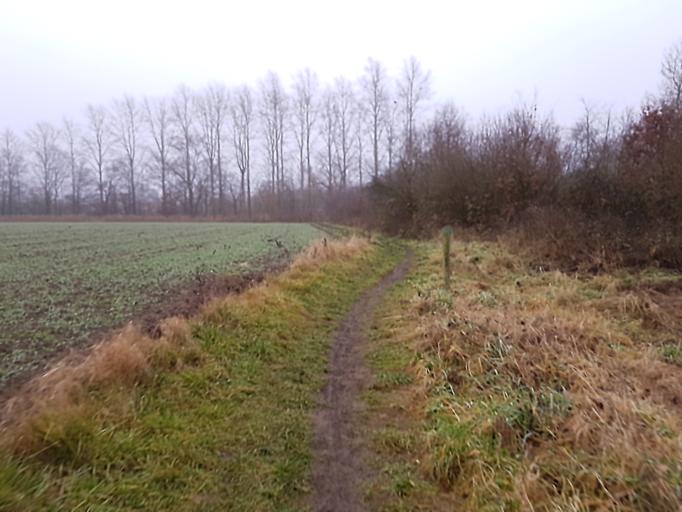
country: BE
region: Flanders
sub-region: Provincie Vlaams-Brabant
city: Boortmeerbeek
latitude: 50.9967
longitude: 4.5828
